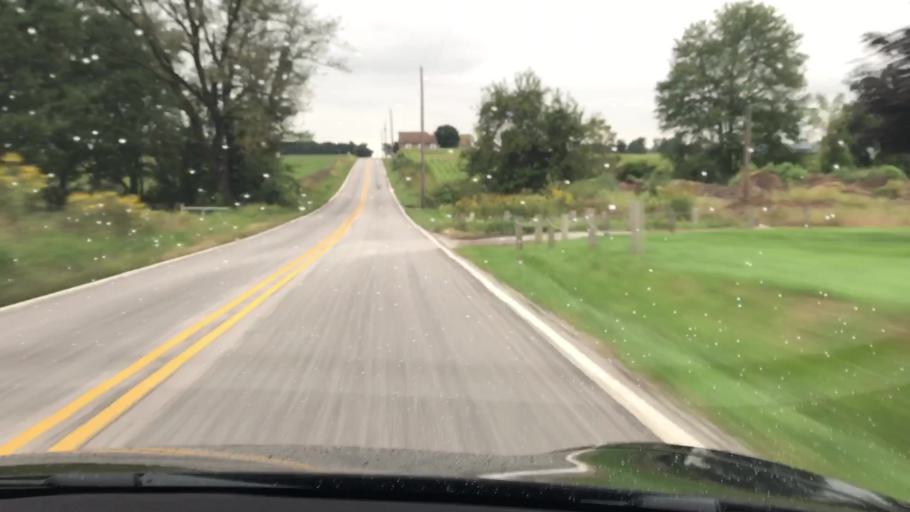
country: US
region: Pennsylvania
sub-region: York County
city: Dover
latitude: 39.9669
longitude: -76.8750
